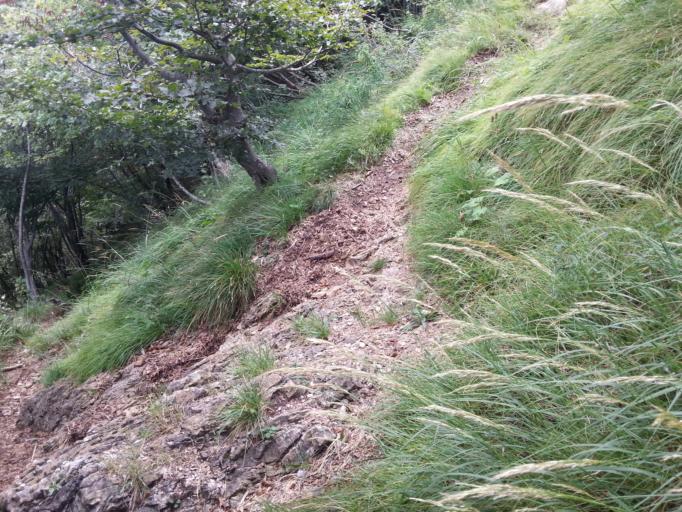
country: IT
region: Lombardy
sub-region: Provincia di Lecco
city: Cortenova
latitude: 45.9923
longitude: 9.3767
